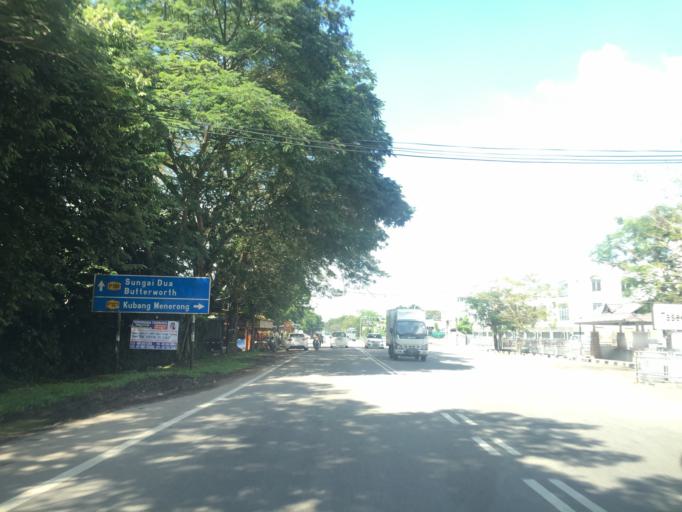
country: MY
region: Penang
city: Tasek Glugor
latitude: 5.4845
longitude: 100.4875
